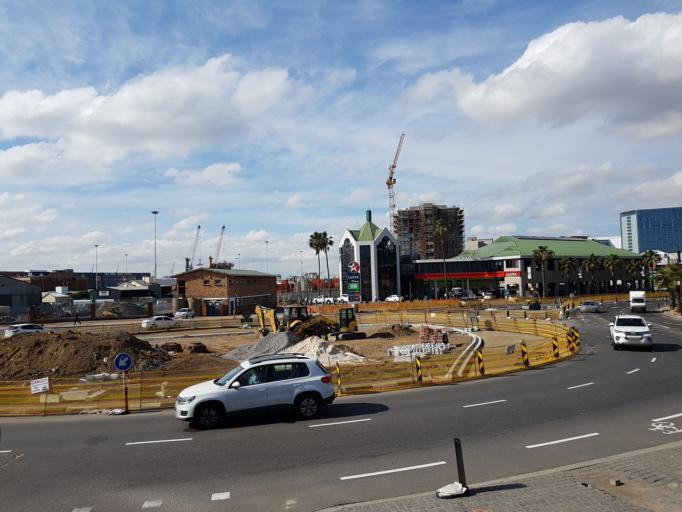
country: ZA
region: Western Cape
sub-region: City of Cape Town
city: Cape Town
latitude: -33.9115
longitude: 18.4220
